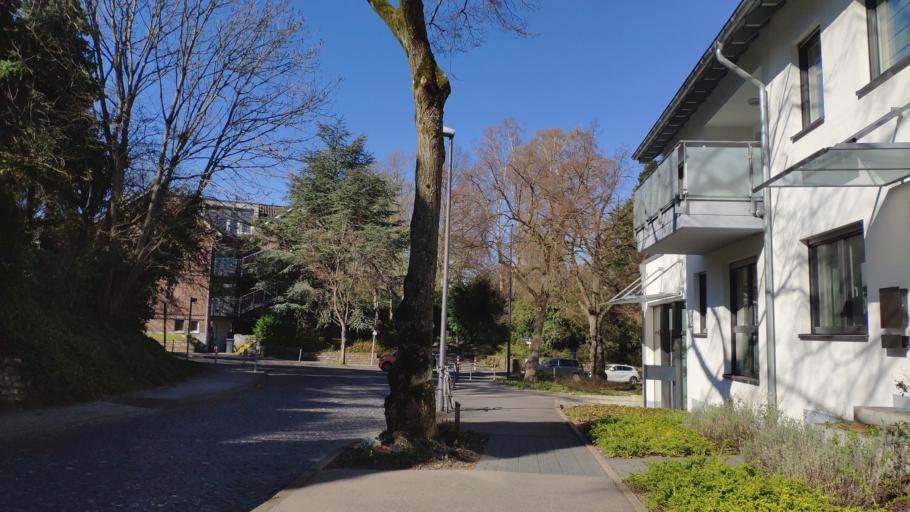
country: DE
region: North Rhine-Westphalia
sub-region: Regierungsbezirk Koln
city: Aachen
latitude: 50.8024
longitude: 6.0545
